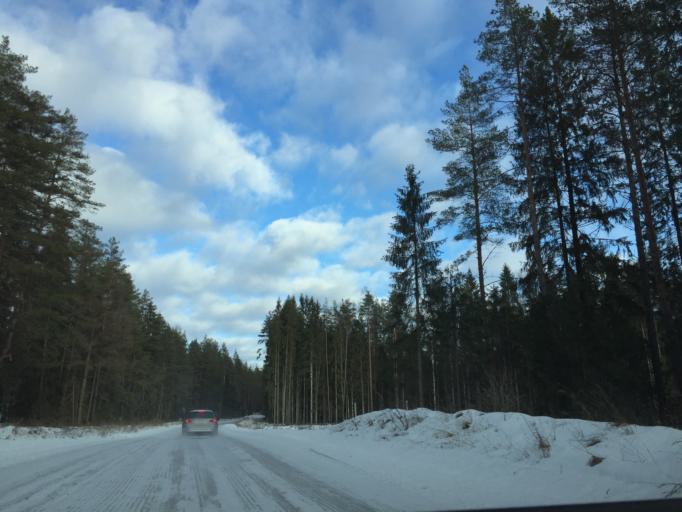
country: LV
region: Ogre
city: Jumprava
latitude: 56.5731
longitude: 24.9375
